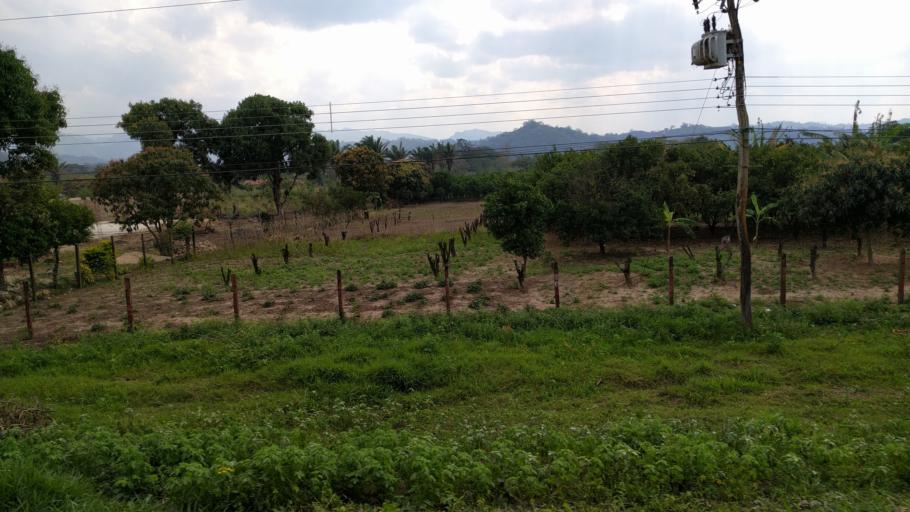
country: BO
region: Santa Cruz
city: Jorochito
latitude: -18.0615
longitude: -63.4327
